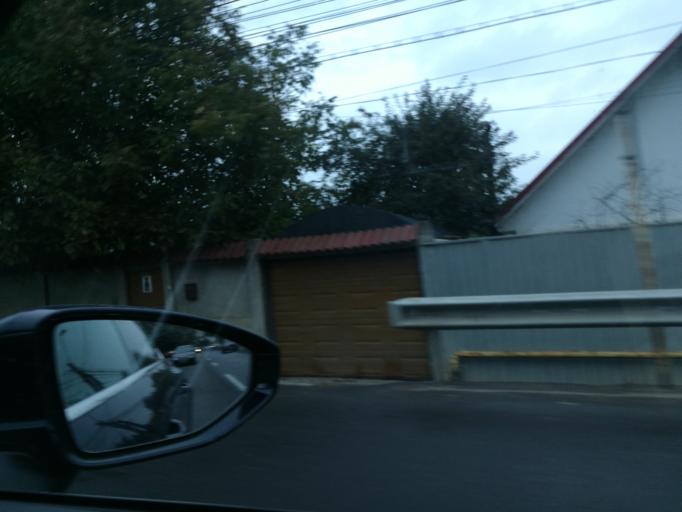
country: RO
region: Galati
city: Galati
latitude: 45.4695
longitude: 28.0342
